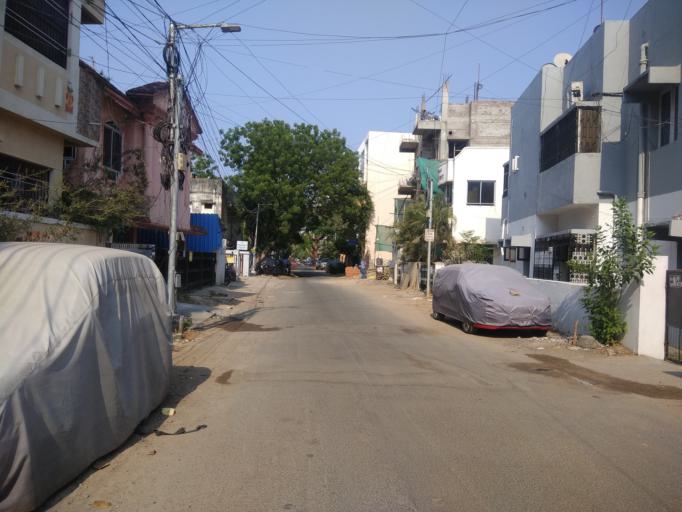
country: IN
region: Tamil Nadu
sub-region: Chennai
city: Gandhi Nagar
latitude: 13.0338
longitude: 80.2343
